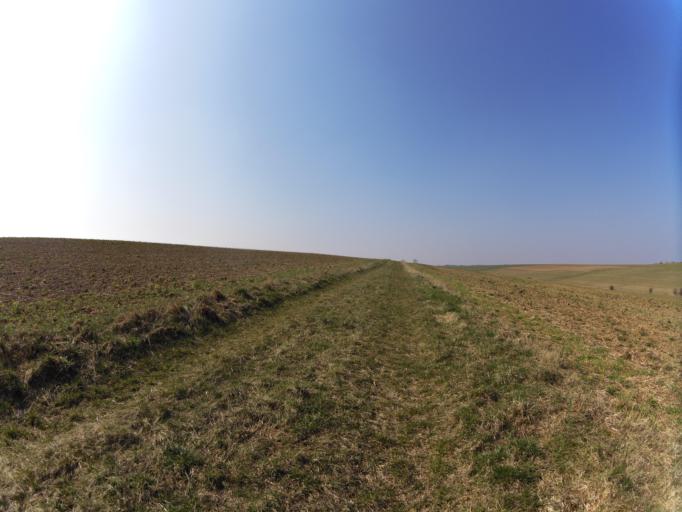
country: DE
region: Bavaria
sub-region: Regierungsbezirk Unterfranken
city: Winterhausen
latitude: 49.6782
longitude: 9.9861
